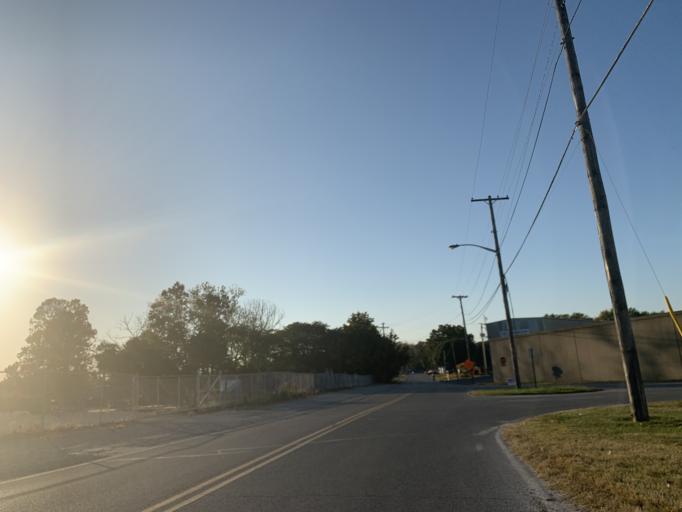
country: US
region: Kentucky
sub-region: Jefferson County
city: Louisville
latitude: 38.2694
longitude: -85.7520
